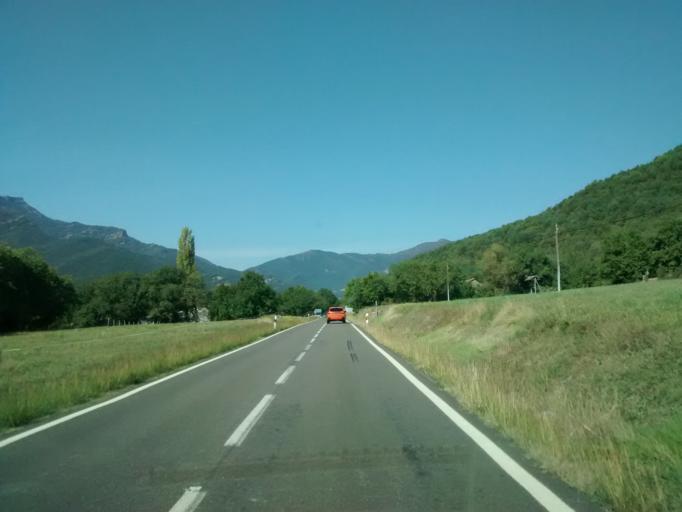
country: ES
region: Aragon
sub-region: Provincia de Huesca
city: Fiscal
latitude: 42.4783
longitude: -0.0702
